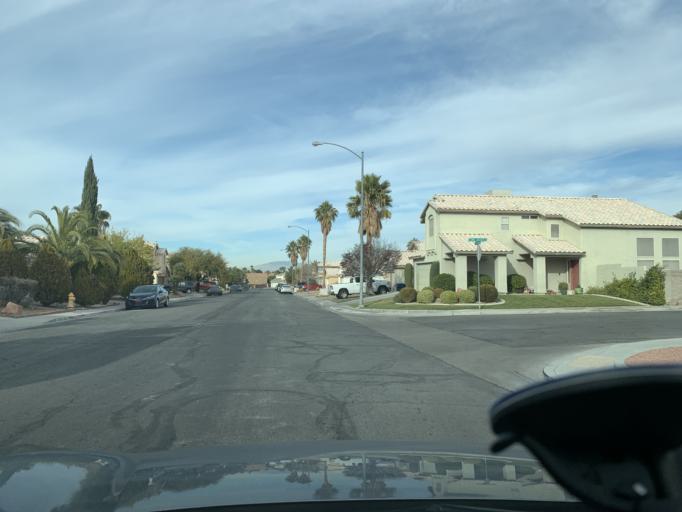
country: US
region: Nevada
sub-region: Clark County
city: Spring Valley
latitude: 36.0889
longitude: -115.2660
